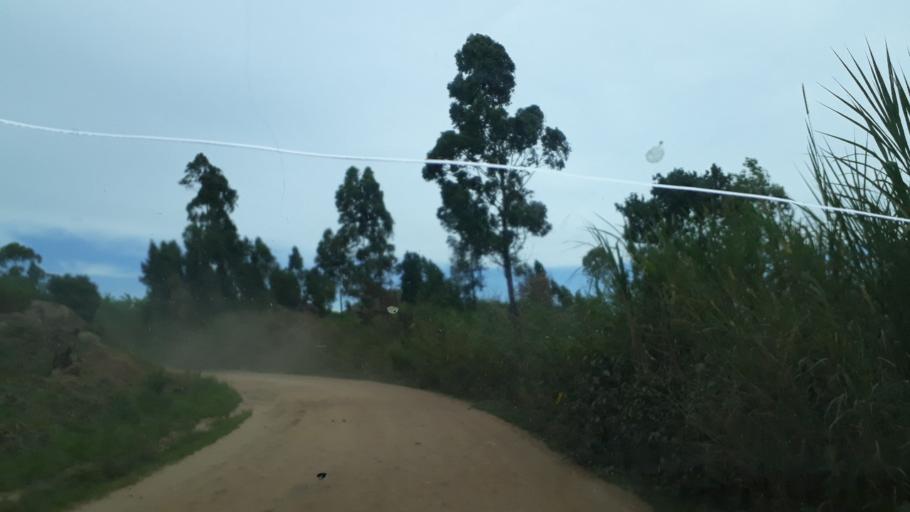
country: CD
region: Eastern Province
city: Bunia
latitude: 1.8959
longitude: 30.4924
